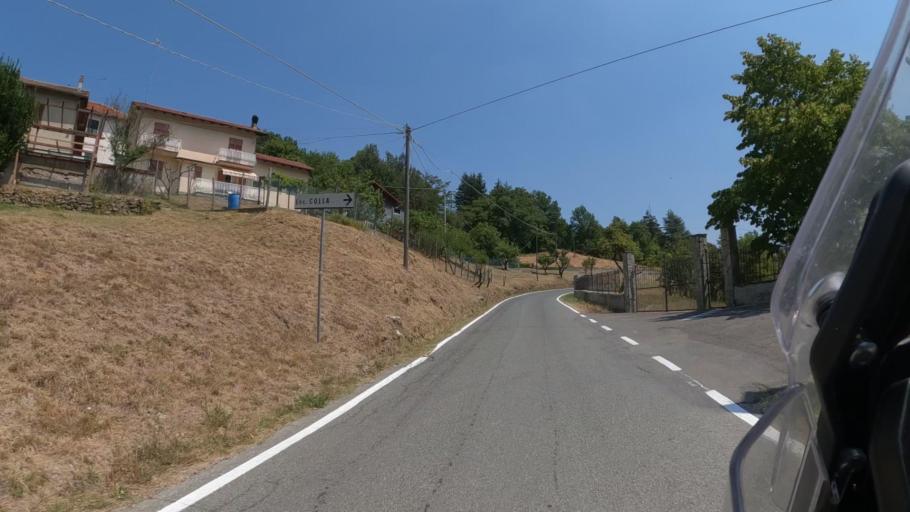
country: IT
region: Piedmont
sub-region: Provincia di Alessandria
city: Cassinelle-Concentrico
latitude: 44.5789
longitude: 8.5464
